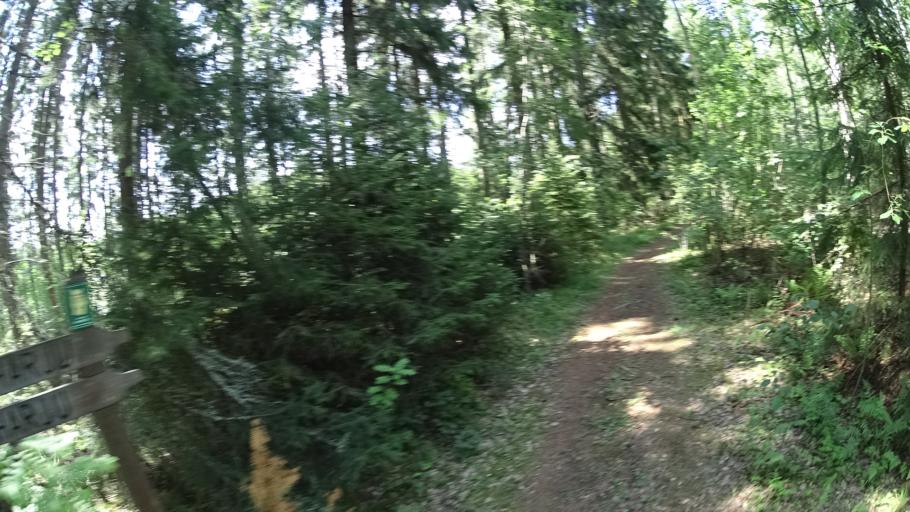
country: FI
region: Haeme
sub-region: Forssa
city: Tammela
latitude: 60.7716
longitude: 23.8646
